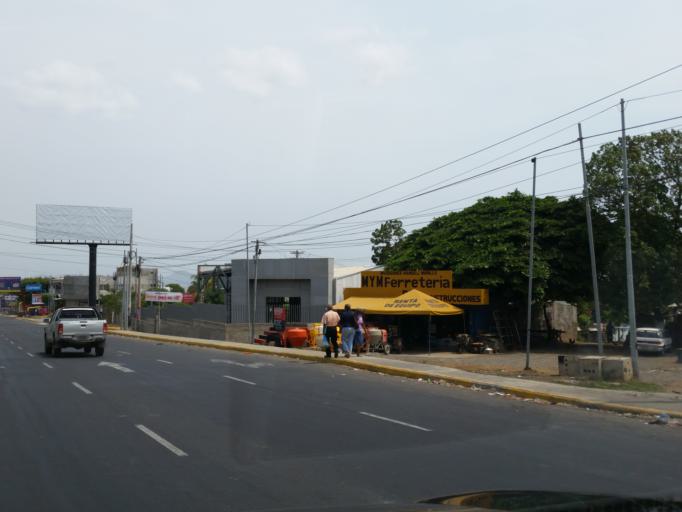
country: NI
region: Managua
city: Managua
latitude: 12.1086
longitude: -86.2509
